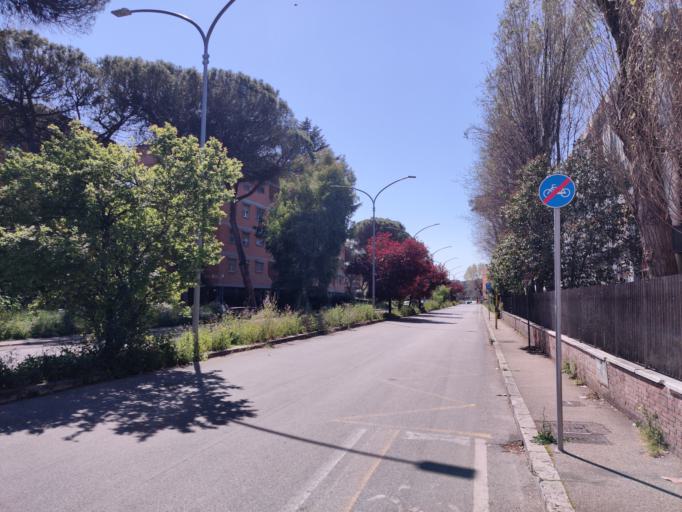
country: IT
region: Latium
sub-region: Citta metropolitana di Roma Capitale
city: Vitinia
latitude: 41.8208
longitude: 12.4434
